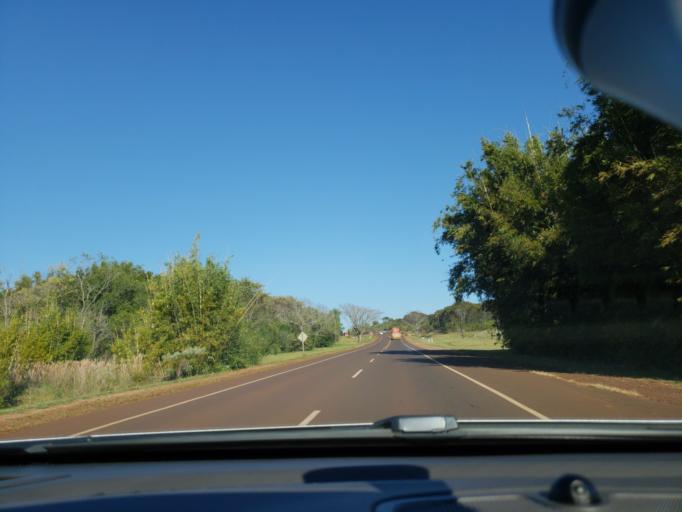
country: AR
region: Misiones
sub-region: Departamento de Apostoles
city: San Jose
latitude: -27.7940
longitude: -55.7713
